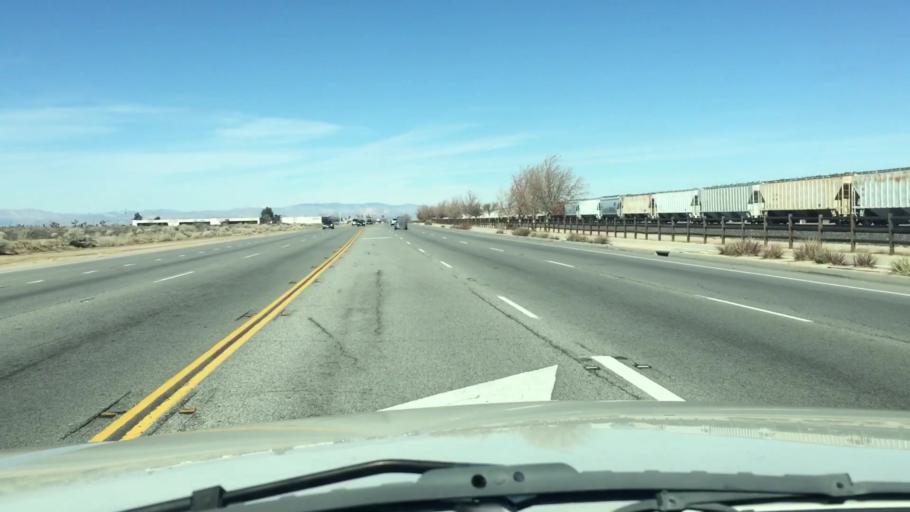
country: US
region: California
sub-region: Los Angeles County
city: Desert View Highlands
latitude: 34.6323
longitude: -118.1261
